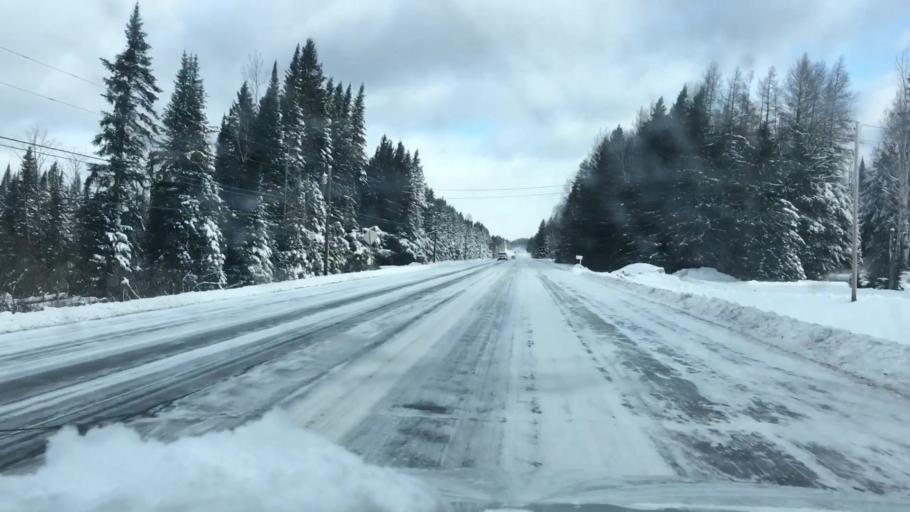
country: US
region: Maine
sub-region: Aroostook County
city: Madawaska
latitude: 47.0163
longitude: -68.0165
